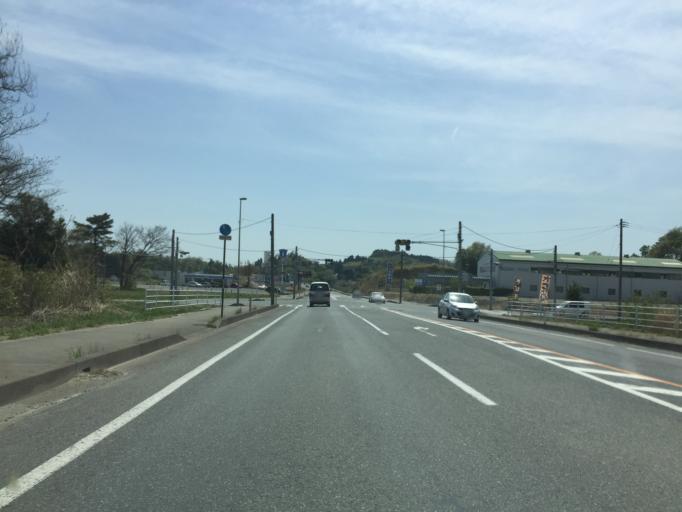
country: JP
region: Miyagi
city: Marumori
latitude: 37.8607
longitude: 140.9203
